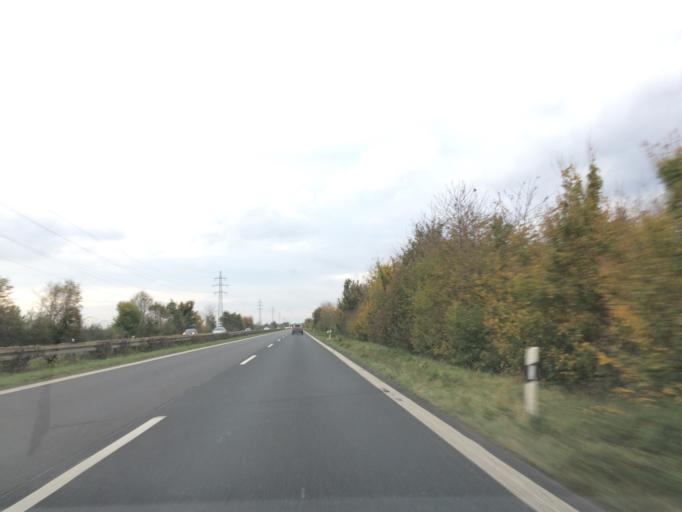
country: DE
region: Bavaria
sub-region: Regierungsbezirk Unterfranken
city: Niedernberg
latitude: 49.9013
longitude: 9.1260
